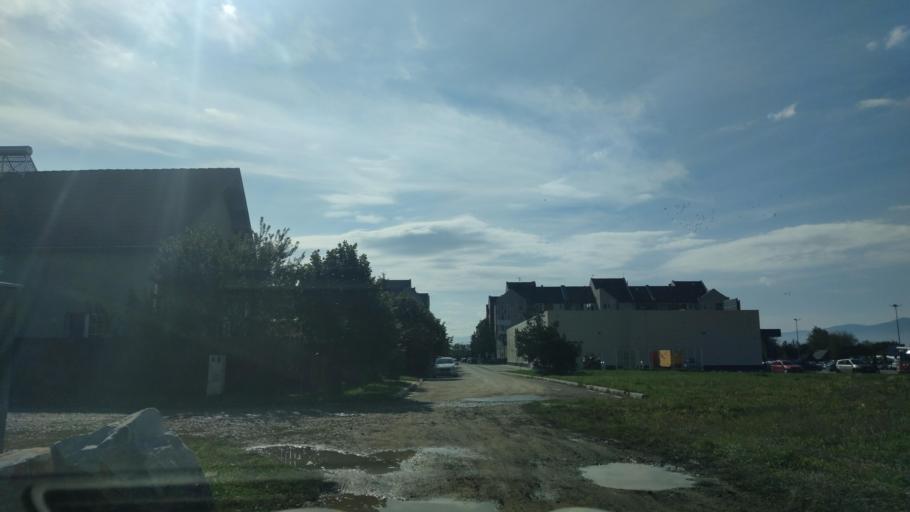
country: RO
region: Harghita
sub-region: Municipiul Gheorgheni
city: Gheorgheni
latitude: 46.7225
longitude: 25.5837
